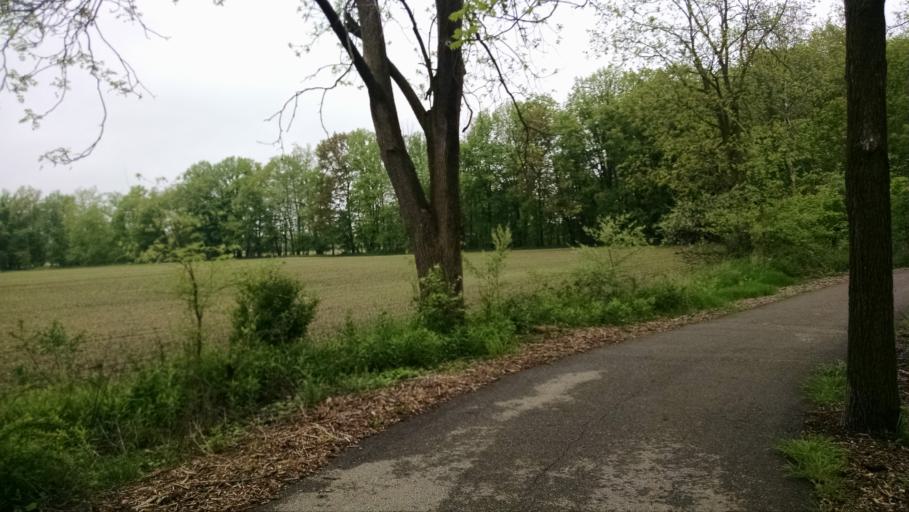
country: US
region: Michigan
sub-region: Eaton County
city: Waverly
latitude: 42.7689
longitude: -84.6367
